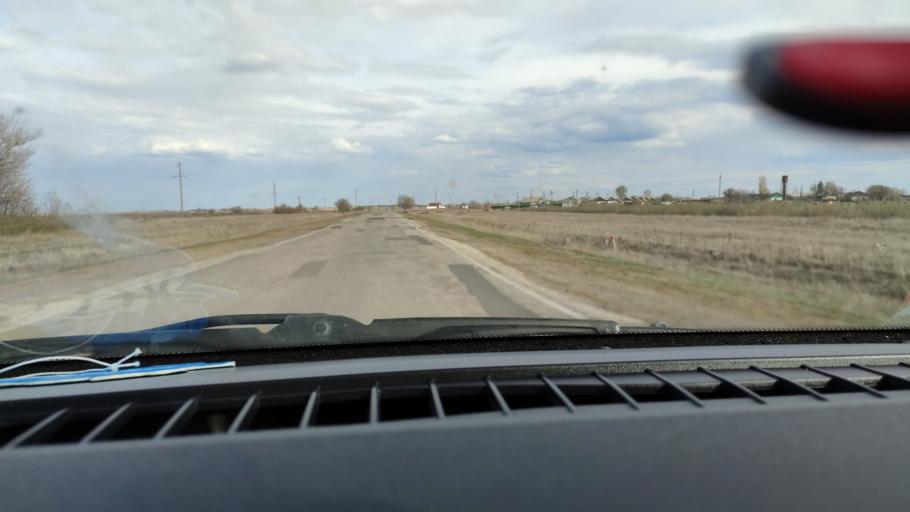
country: RU
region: Saratov
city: Rovnoye
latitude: 51.0616
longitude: 46.0207
